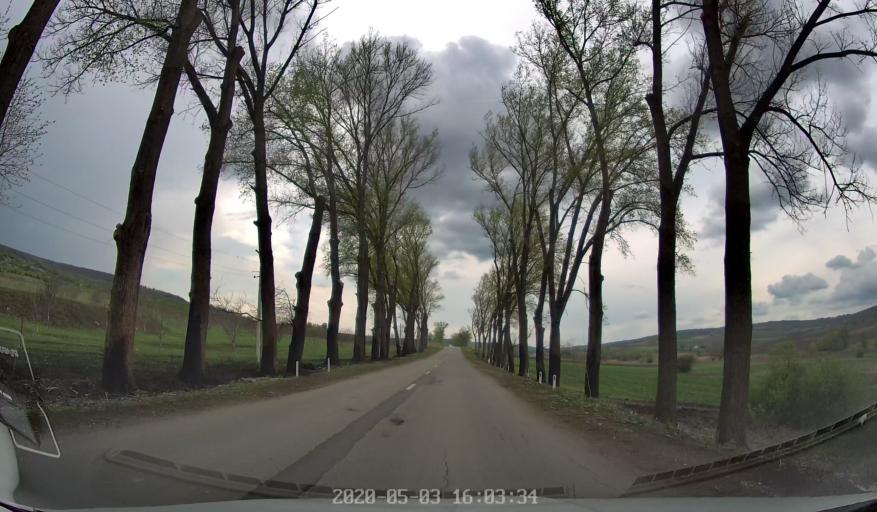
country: MD
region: Stinga Nistrului
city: Bucovat
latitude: 47.1808
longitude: 28.3794
